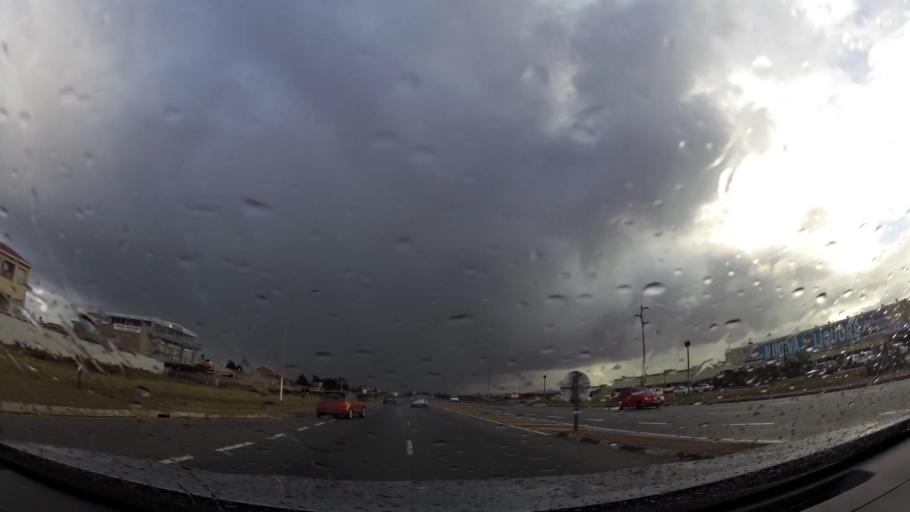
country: ZA
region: Western Cape
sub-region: Eden District Municipality
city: Mossel Bay
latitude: -34.1833
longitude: 22.1134
